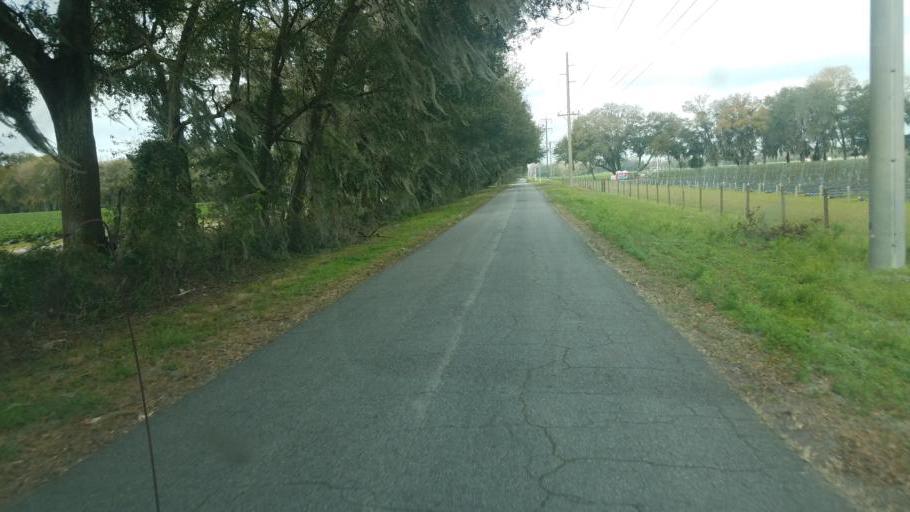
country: US
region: Florida
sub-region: Polk County
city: Willow Oak
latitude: 27.9271
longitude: -82.0785
